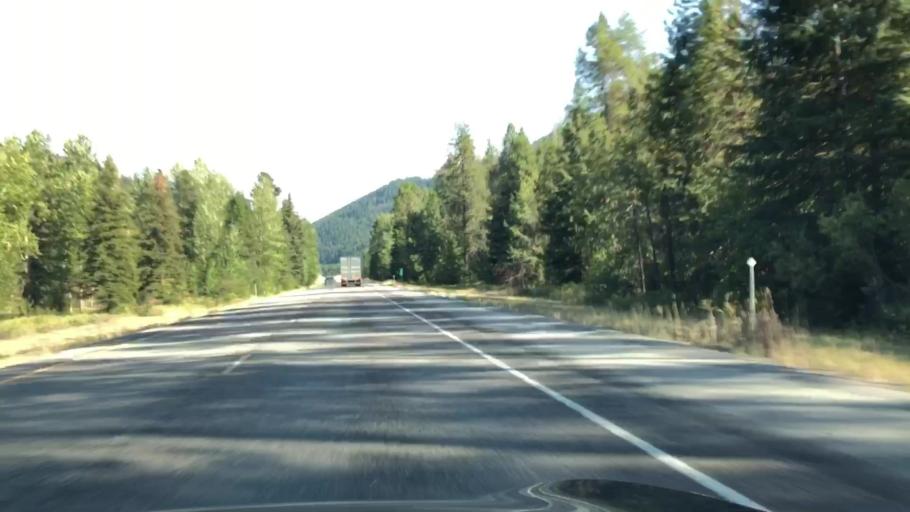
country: US
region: Montana
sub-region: Sanders County
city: Thompson Falls
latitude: 47.3673
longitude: -115.3326
